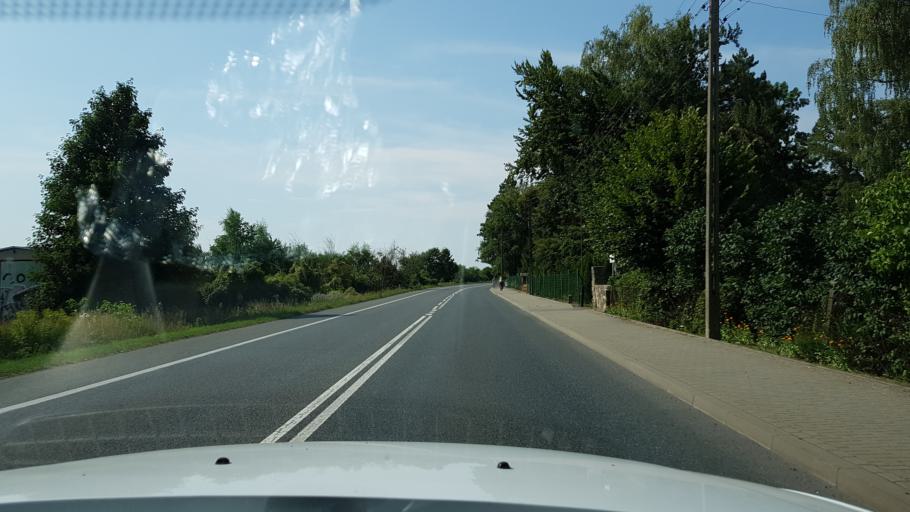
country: PL
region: West Pomeranian Voivodeship
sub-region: Powiat pyrzycki
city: Lipiany
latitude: 53.0044
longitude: 14.9509
